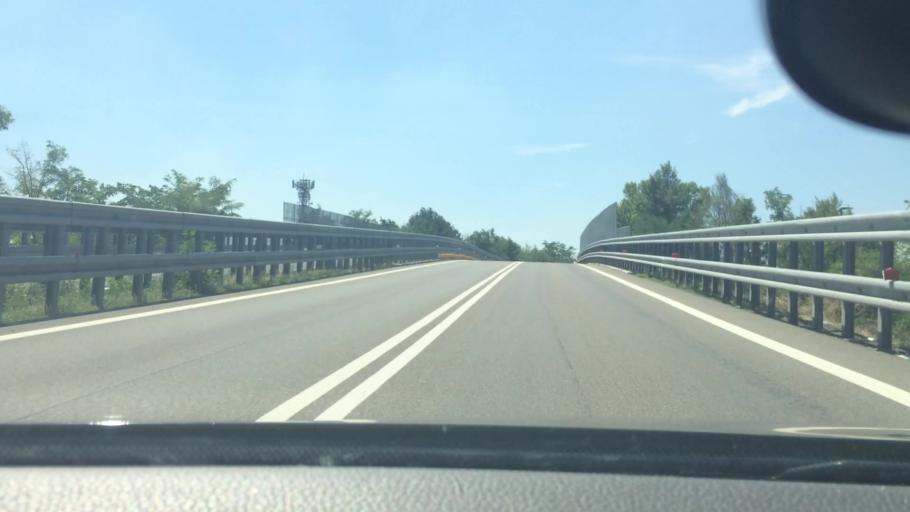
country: IT
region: Lombardy
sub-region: Provincia di Lodi
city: San Rocco al Porto
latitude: 45.0579
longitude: 9.6592
